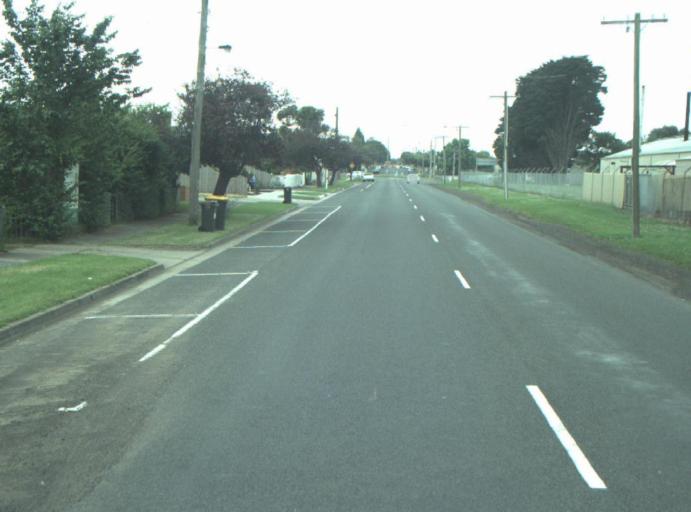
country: AU
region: Victoria
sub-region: Greater Geelong
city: Breakwater
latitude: -38.1702
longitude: 144.3722
